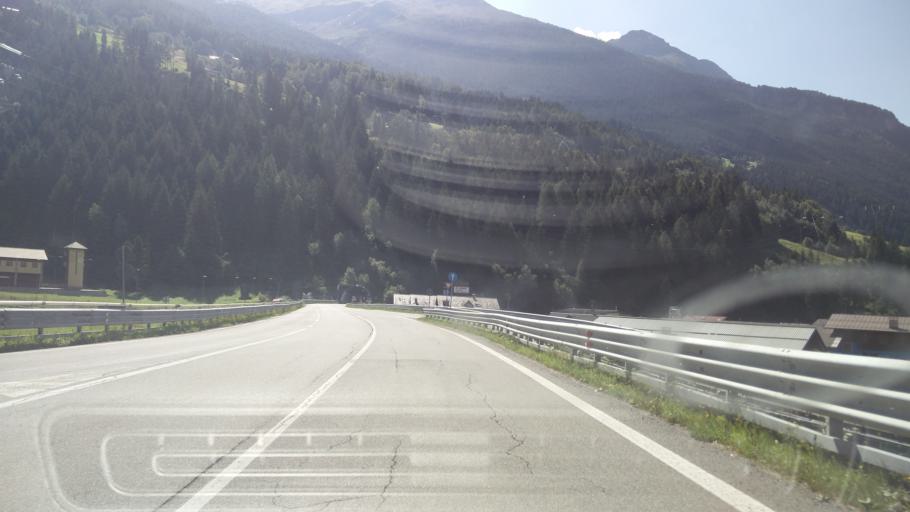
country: IT
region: Lombardy
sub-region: Provincia di Sondrio
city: Cepina
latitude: 46.4491
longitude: 10.3618
